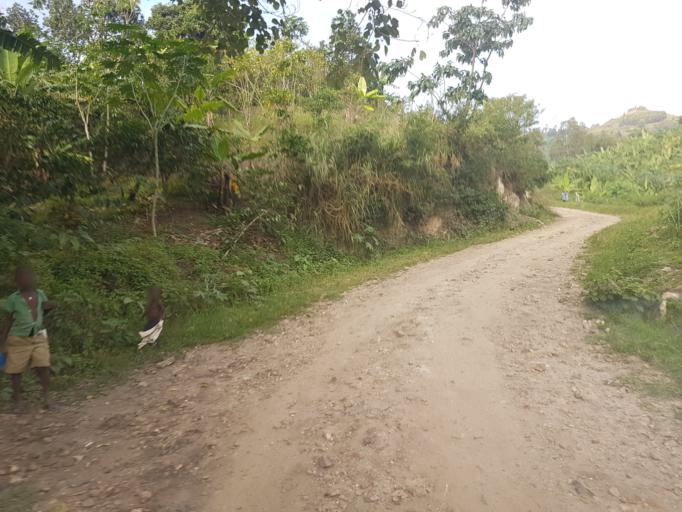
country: UG
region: Western Region
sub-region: Rukungiri District
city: Rukungiri
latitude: -0.6761
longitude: 29.8989
